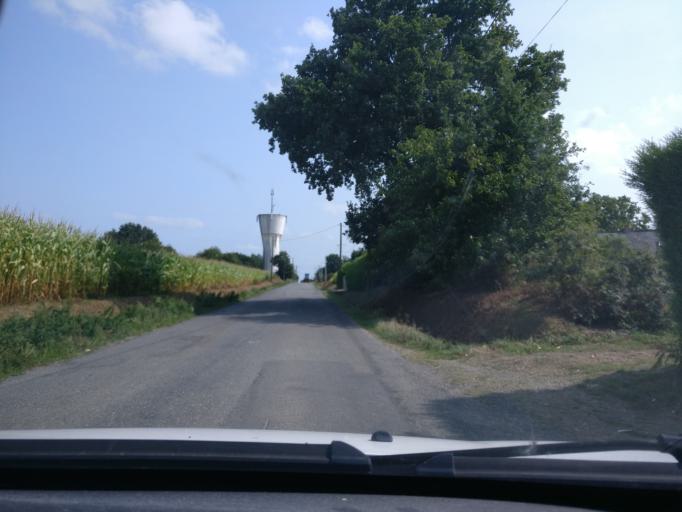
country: FR
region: Brittany
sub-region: Departement d'Ille-et-Vilaine
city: Gosne
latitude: 48.2514
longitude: -1.4762
